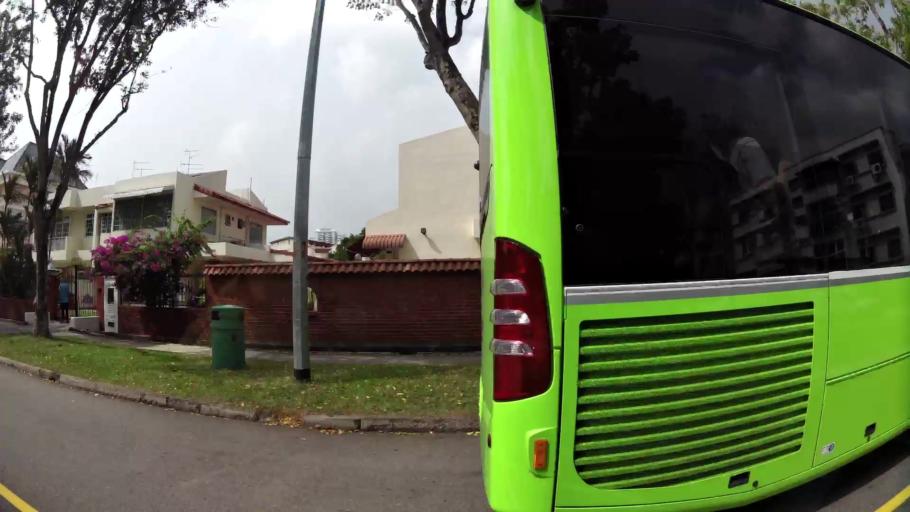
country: SG
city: Singapore
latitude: 1.3079
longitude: 103.9127
